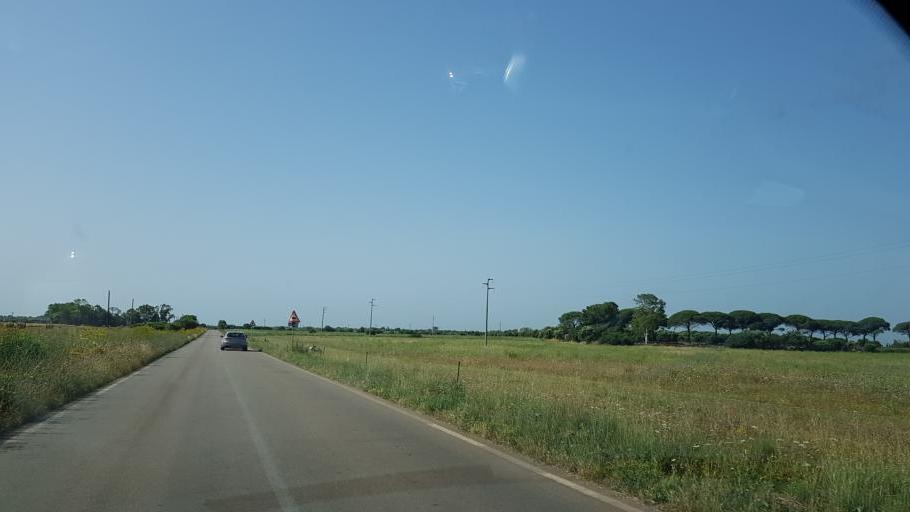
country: IT
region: Apulia
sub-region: Provincia di Brindisi
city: San Pancrazio Salentino
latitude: 40.3425
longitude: 17.8483
